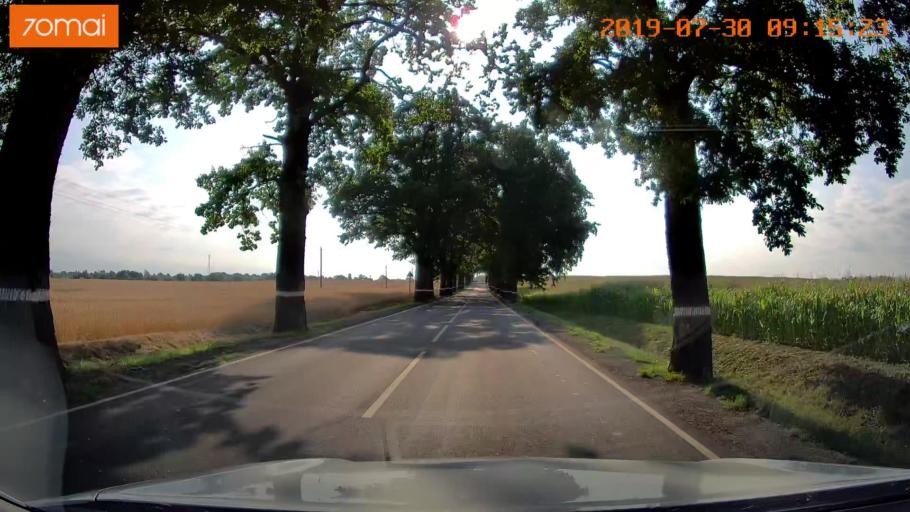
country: RU
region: Kaliningrad
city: Nesterov
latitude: 54.6339
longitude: 22.5387
